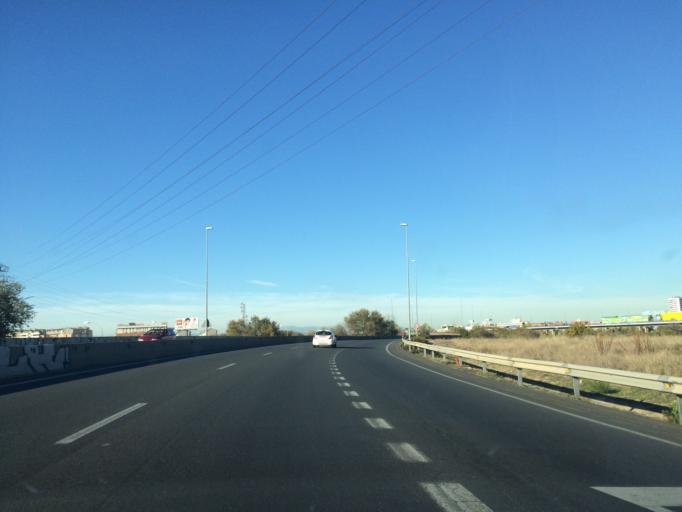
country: ES
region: Madrid
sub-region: Provincia de Madrid
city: Mostoles
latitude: 40.3318
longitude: -3.8526
